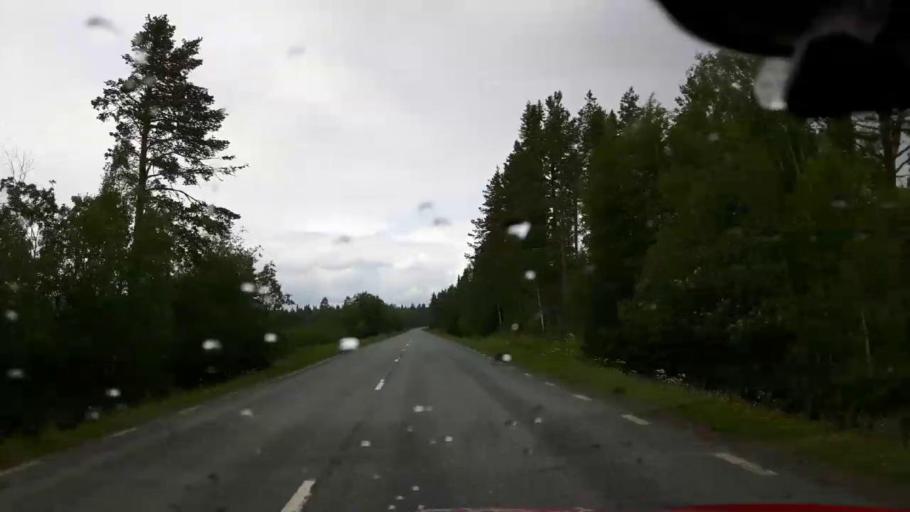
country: SE
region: Jaemtland
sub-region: Krokoms Kommun
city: Krokom
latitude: 63.4413
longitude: 14.1984
